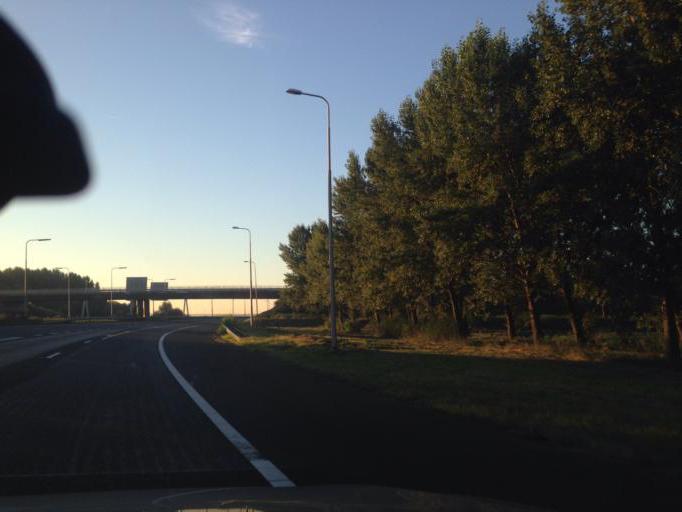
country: NL
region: Flevoland
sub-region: Gemeente Almere
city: Almere Stad
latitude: 52.3780
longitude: 5.3035
